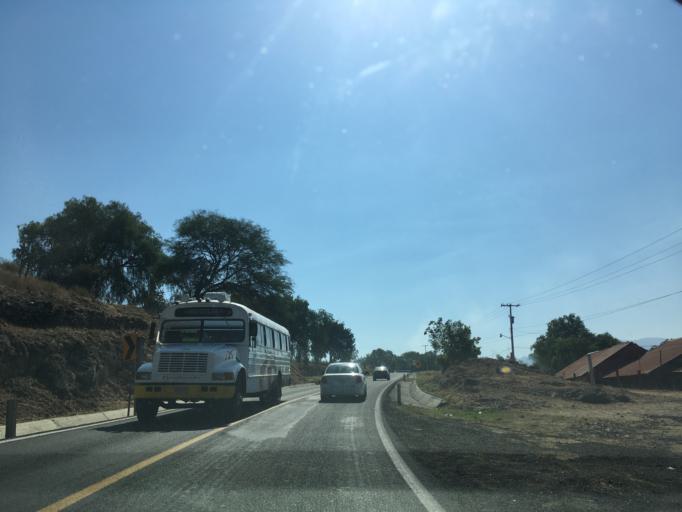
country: MX
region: Michoacan
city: Charo
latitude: 19.7549
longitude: -101.0427
